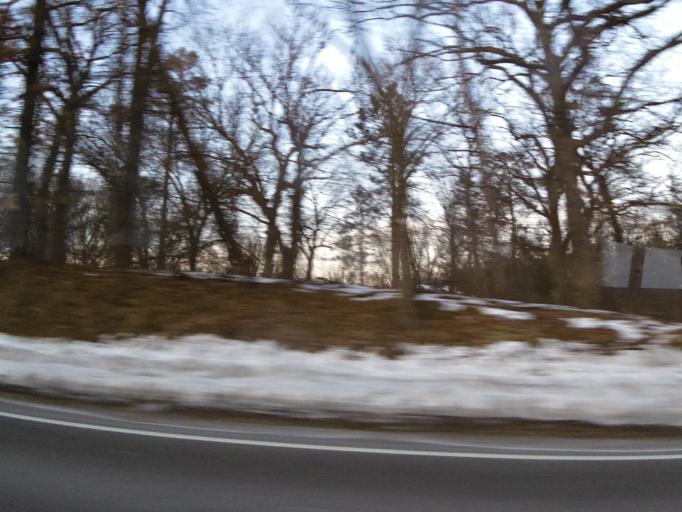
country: US
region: Minnesota
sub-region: Washington County
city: Dellwood
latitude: 45.0902
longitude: -92.9592
